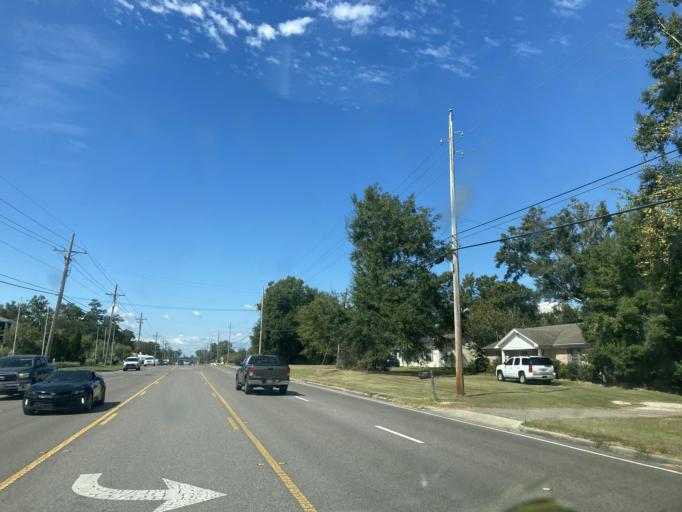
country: US
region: Mississippi
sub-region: Jackson County
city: Saint Martin
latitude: 30.4431
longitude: -88.8560
